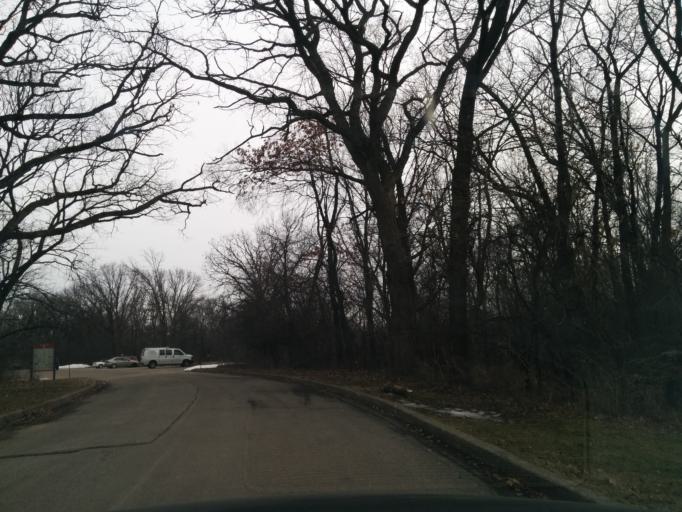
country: US
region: Illinois
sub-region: Cook County
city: Western Springs
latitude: 41.8229
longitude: -87.9073
